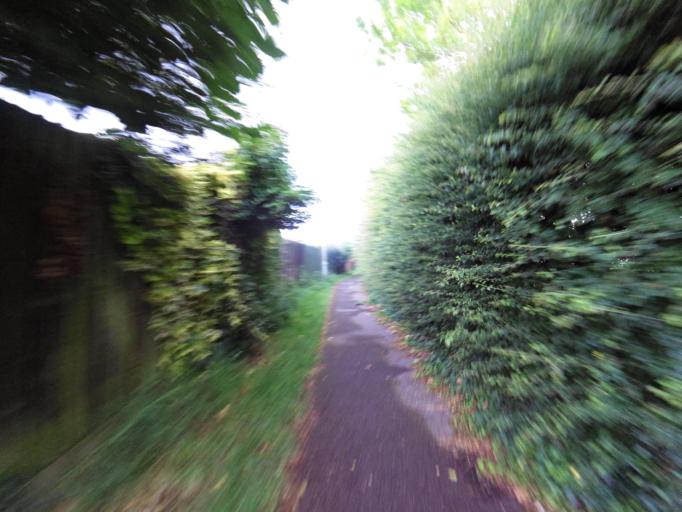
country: GB
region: England
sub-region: Suffolk
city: Bramford
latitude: 52.0755
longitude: 1.1254
